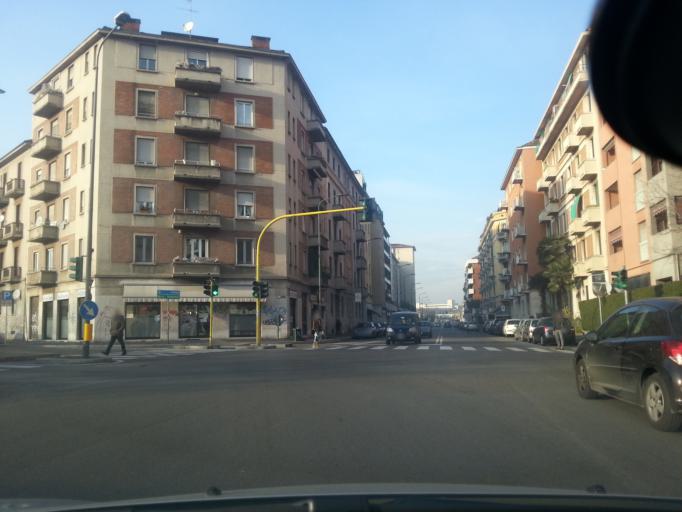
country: IT
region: Lombardy
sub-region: Citta metropolitana di Milano
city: Milano
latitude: 45.5008
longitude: 9.1903
